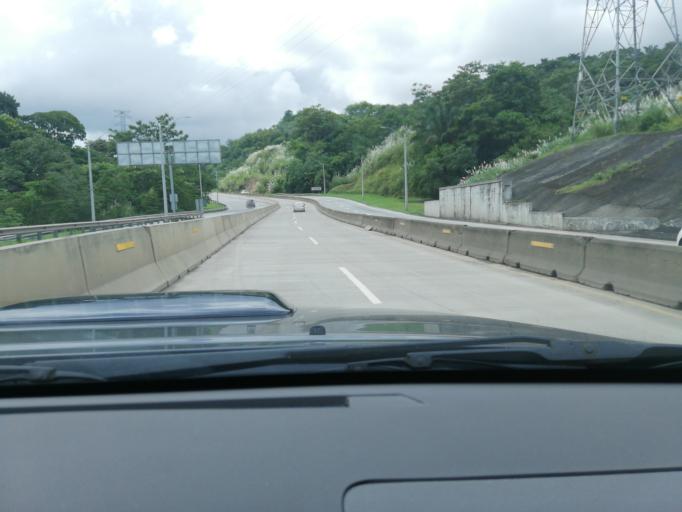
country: PA
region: Panama
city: San Miguelito
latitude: 9.0803
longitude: -79.4621
